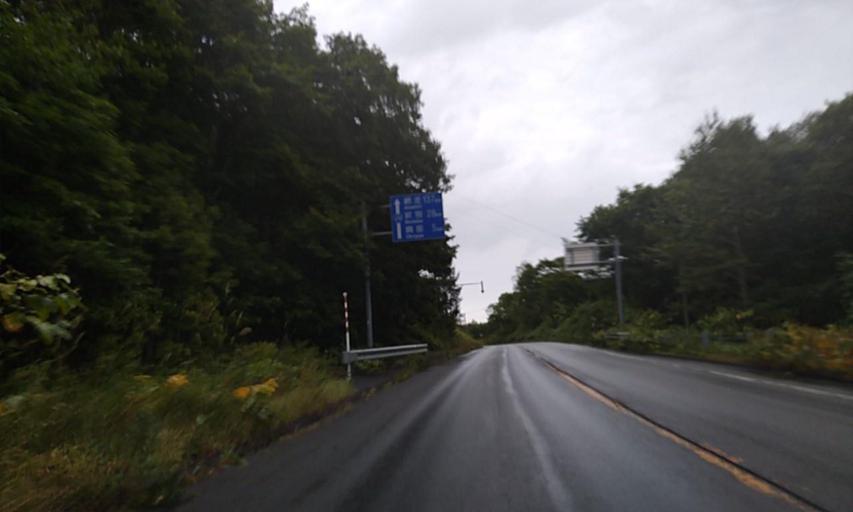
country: JP
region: Hokkaido
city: Mombetsu
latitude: 44.4881
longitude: 143.0807
